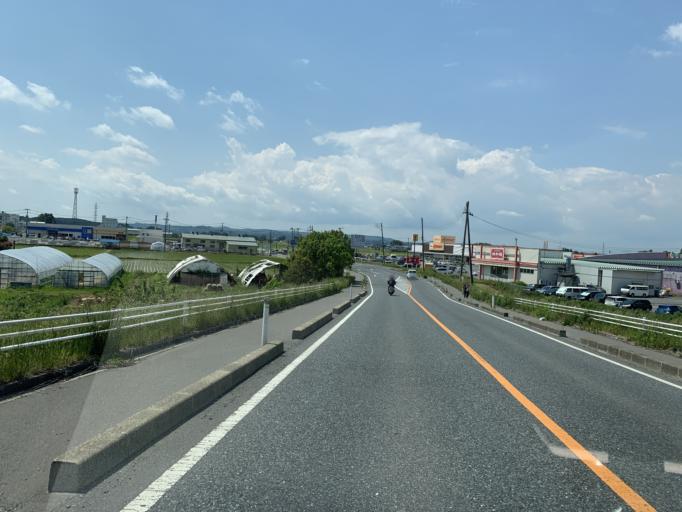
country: JP
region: Miyagi
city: Kogota
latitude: 38.5622
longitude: 141.0447
